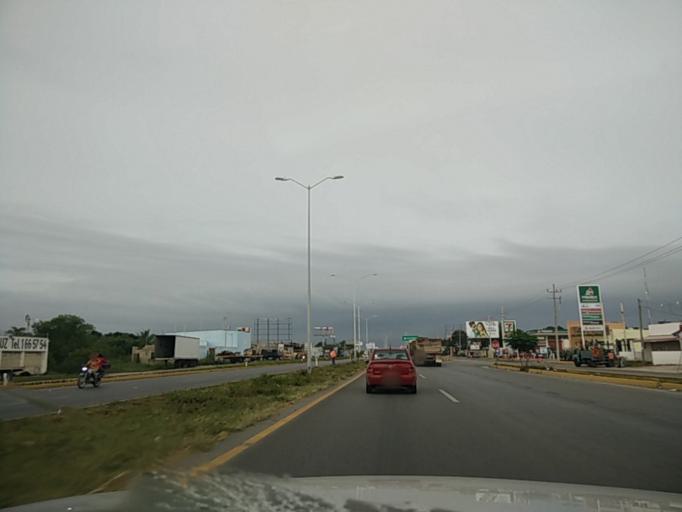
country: MX
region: Yucatan
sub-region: Kanasin
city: Kanasin
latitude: 20.9513
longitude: -89.5612
